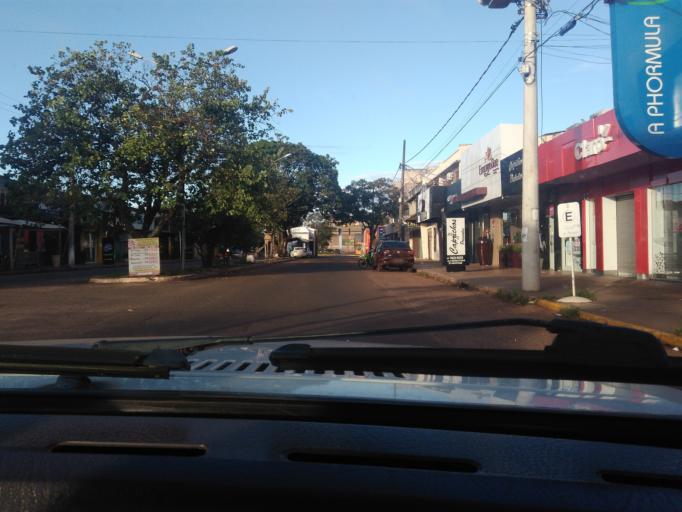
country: BR
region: Mato Grosso do Sul
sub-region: Ponta Pora
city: Ponta Pora
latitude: -22.5373
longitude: -55.7283
